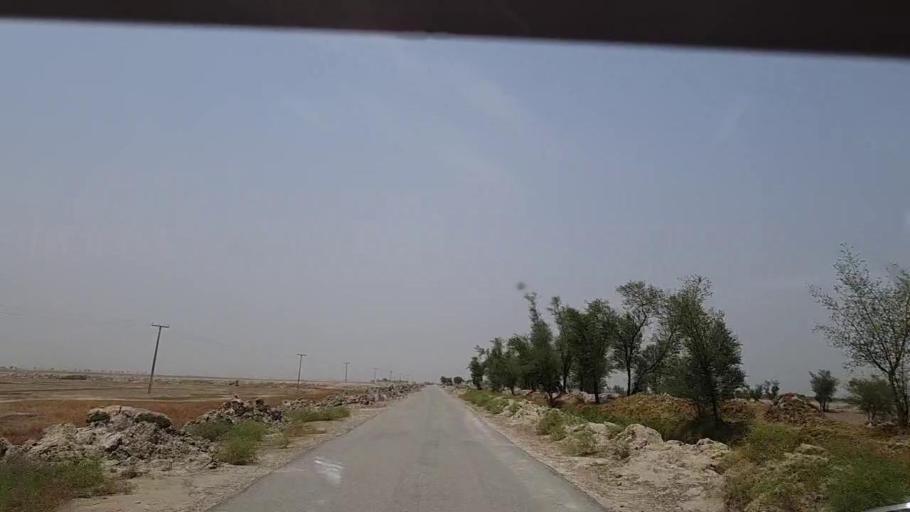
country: PK
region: Sindh
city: Khairpur Nathan Shah
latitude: 27.0315
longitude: 67.6198
